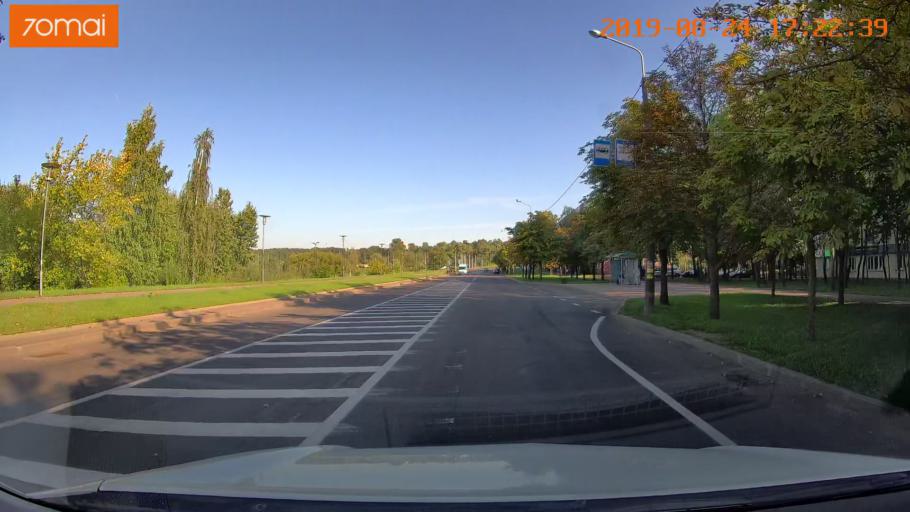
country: BY
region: Minsk
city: Hatava
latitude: 53.8448
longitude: 27.6464
